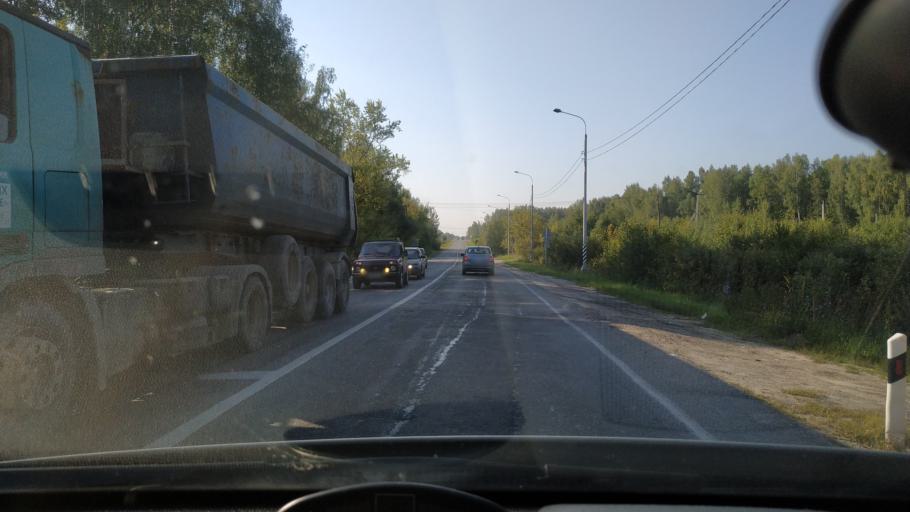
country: RU
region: Moskovskaya
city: Tugolesskiy Bor
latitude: 55.5599
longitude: 39.7022
